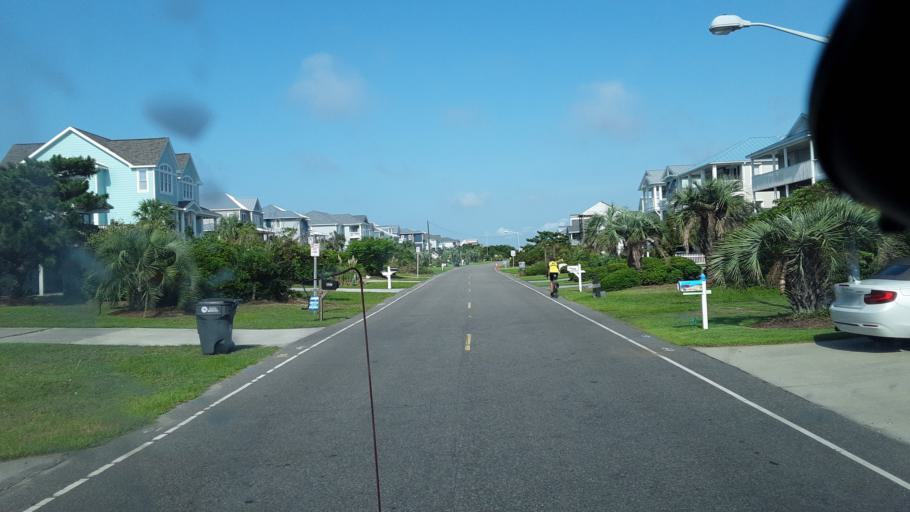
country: US
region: North Carolina
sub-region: Brunswick County
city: Southport
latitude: 33.8942
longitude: -78.0417
